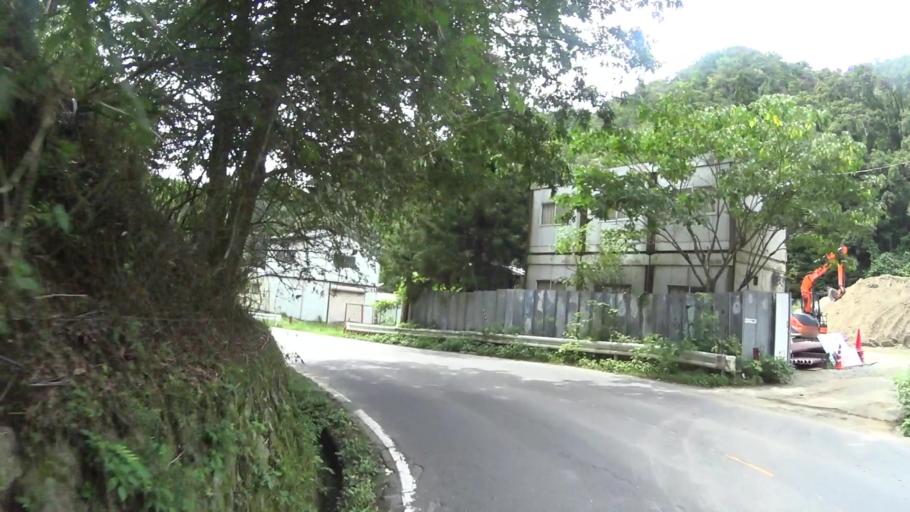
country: JP
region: Kyoto
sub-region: Kyoto-shi
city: Kamigyo-ku
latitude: 35.0403
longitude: 135.8140
